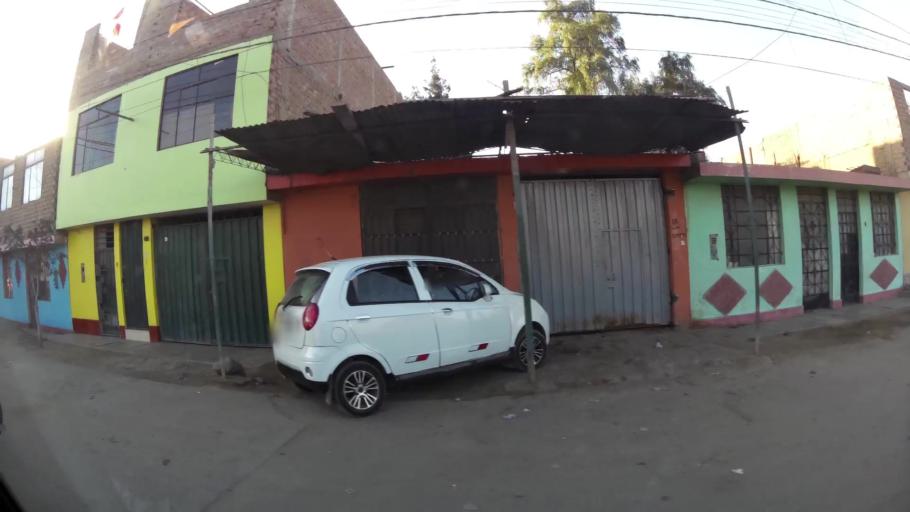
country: PE
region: Ica
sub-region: Provincia de Ica
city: Ica
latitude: -14.0559
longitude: -75.7290
